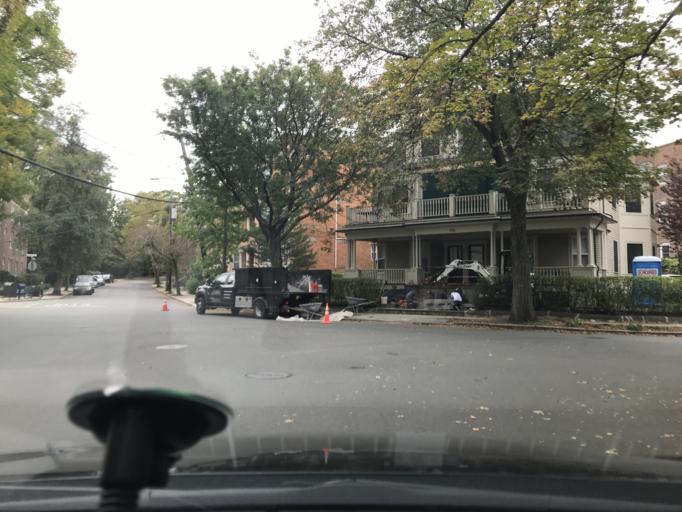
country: US
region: Massachusetts
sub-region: Norfolk County
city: Brookline
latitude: 42.3487
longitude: -71.1243
